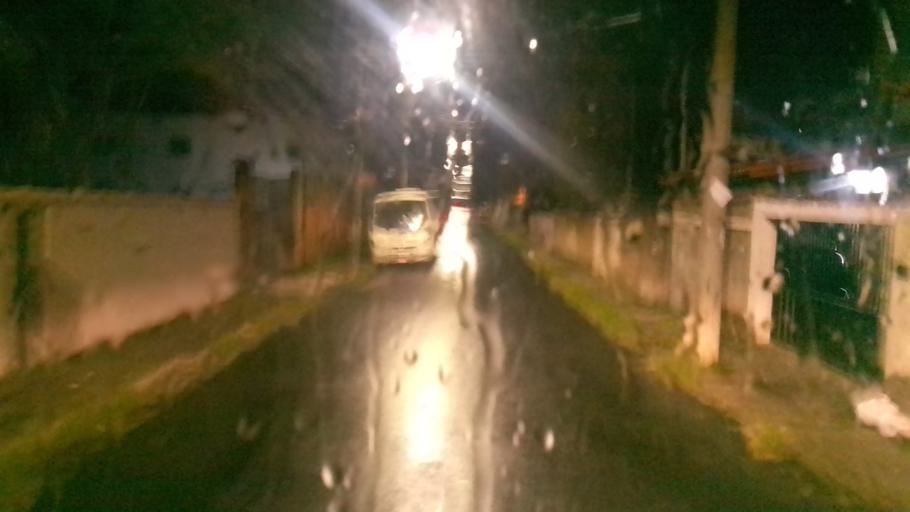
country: BR
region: Minas Gerais
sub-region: Belo Horizonte
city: Belo Horizonte
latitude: -19.8971
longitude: -43.9196
